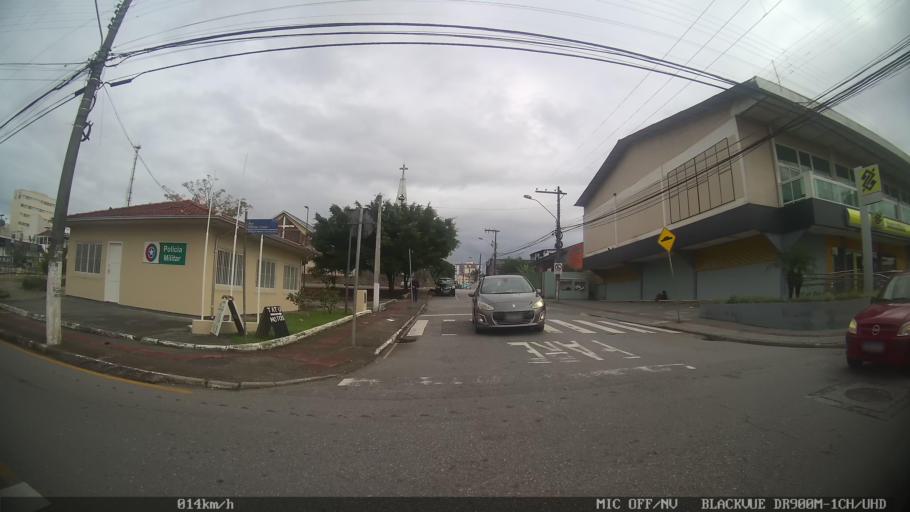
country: BR
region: Santa Catarina
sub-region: Sao Jose
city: Campinas
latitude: -27.5656
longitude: -48.6174
